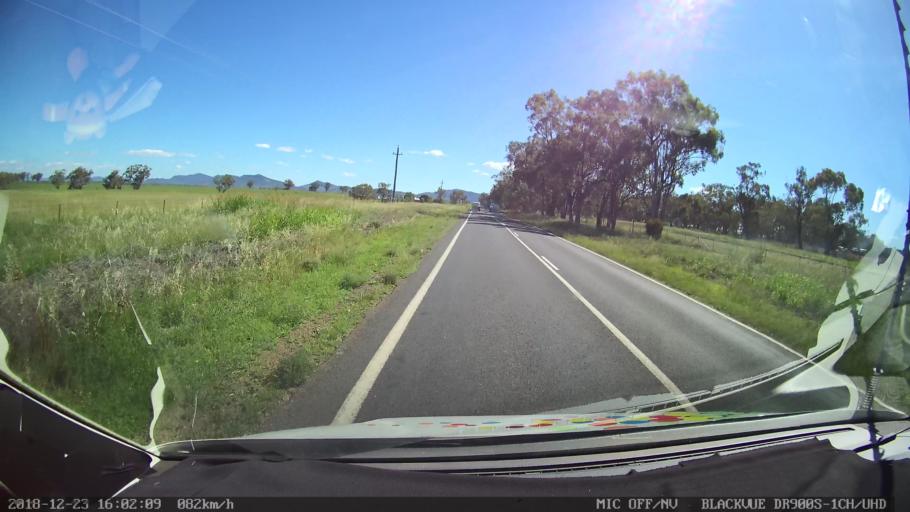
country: AU
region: New South Wales
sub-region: Tamworth Municipality
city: Phillip
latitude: -31.2292
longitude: 150.8113
